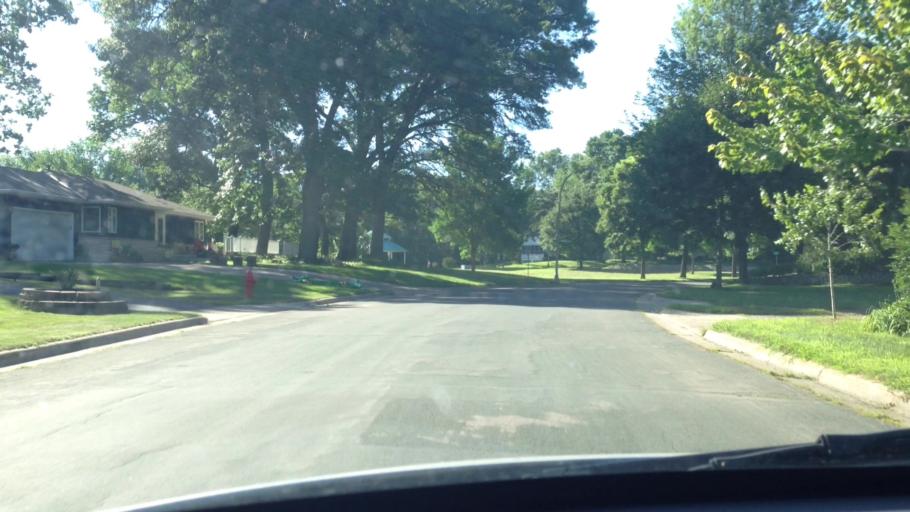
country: US
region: Minnesota
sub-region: Hennepin County
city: Richfield
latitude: 44.8807
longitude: -93.3021
